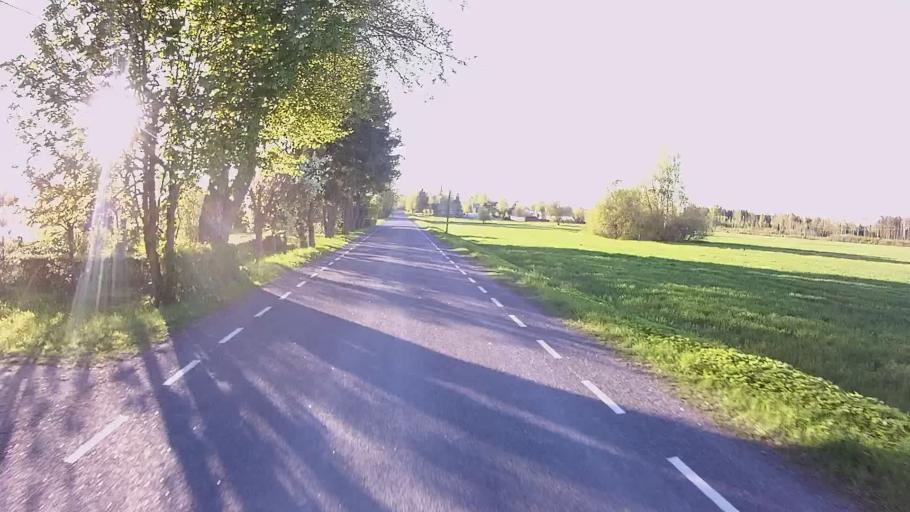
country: EE
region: Jogevamaa
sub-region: Poltsamaa linn
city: Poltsamaa
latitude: 58.5280
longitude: 25.9526
